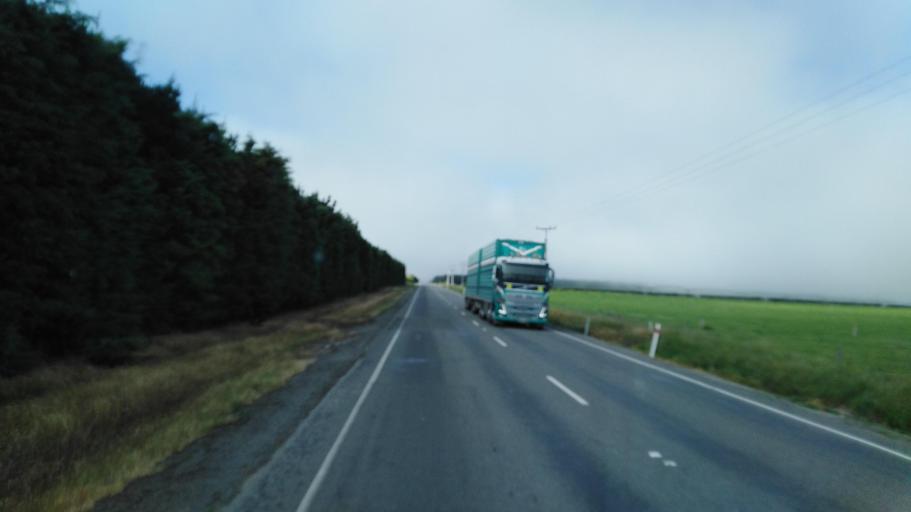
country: NZ
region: Canterbury
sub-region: Hurunui District
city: Amberley
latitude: -42.8087
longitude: 172.8204
